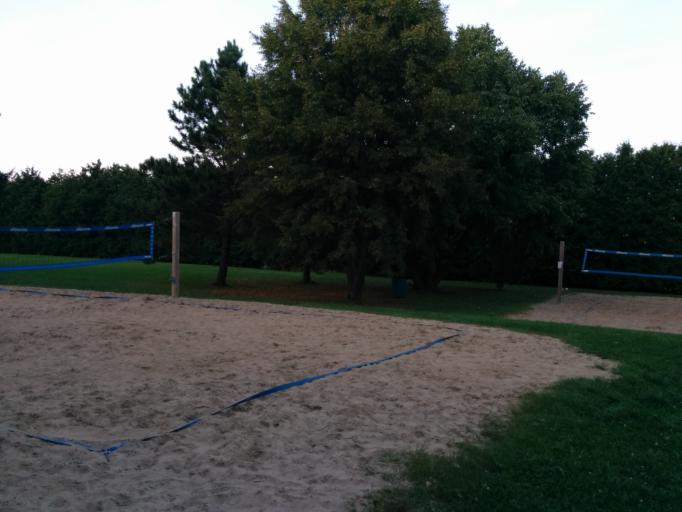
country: CA
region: Ontario
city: Ottawa
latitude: 45.3702
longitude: -75.7281
